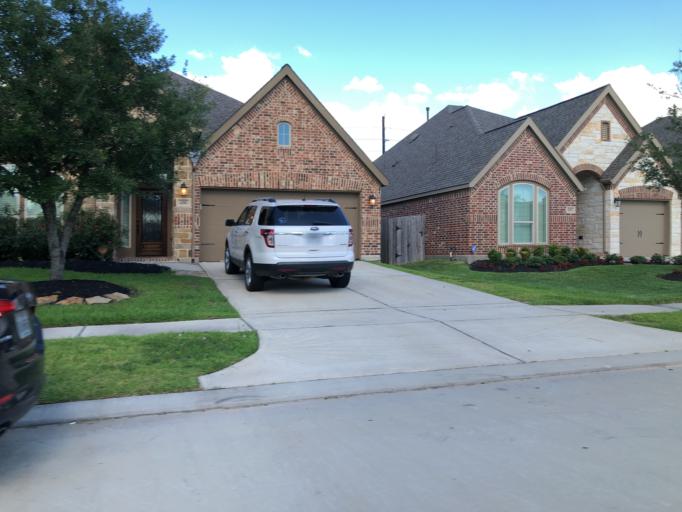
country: US
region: Texas
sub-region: Harris County
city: Katy
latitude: 29.8347
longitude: -95.7742
